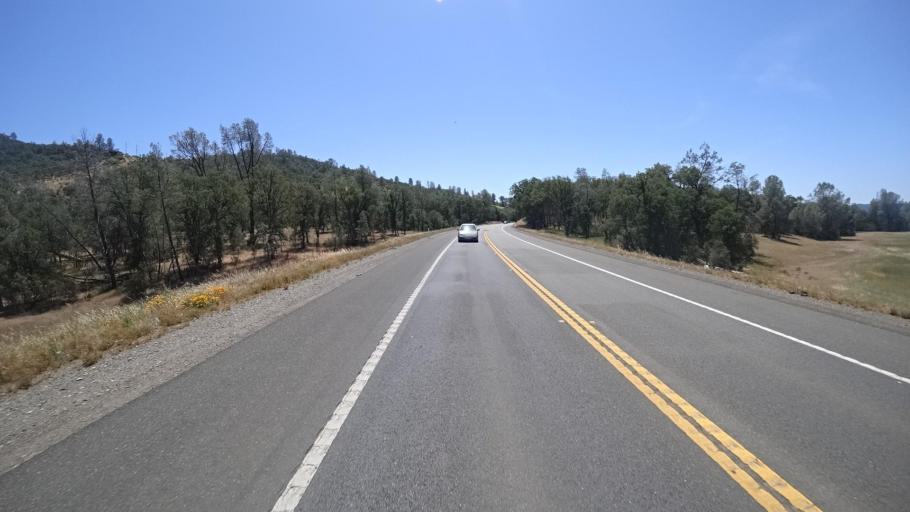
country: US
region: California
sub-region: Lake County
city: Clearlake
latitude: 38.9708
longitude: -122.6130
